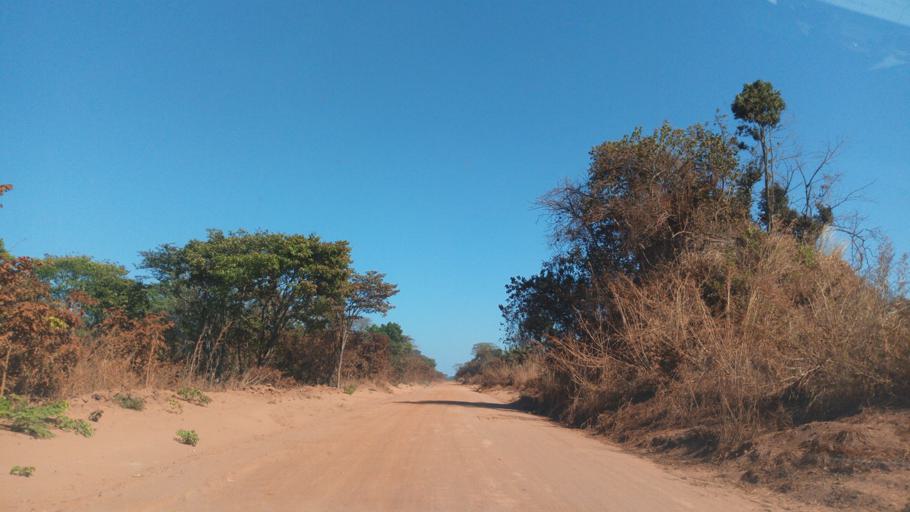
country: ZM
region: Luapula
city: Mwense
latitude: -10.7547
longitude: 28.3144
